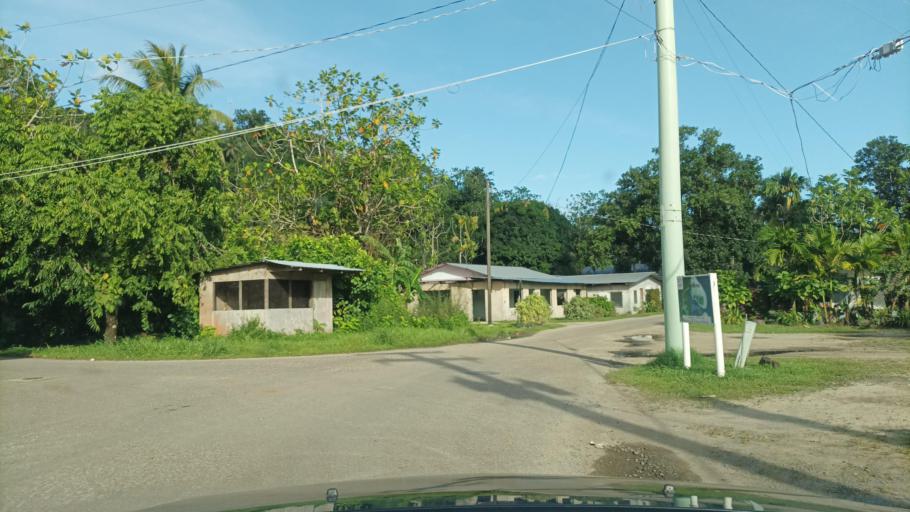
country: FM
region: Kosrae
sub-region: Lelu Municipality
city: Lelu
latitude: 5.3302
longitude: 163.0253
